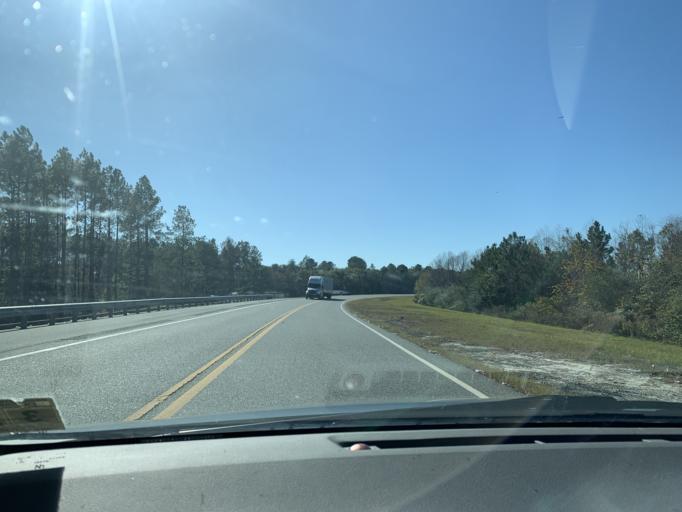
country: US
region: Georgia
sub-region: Atkinson County
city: Willacoochee
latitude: 31.3487
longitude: -83.0127
